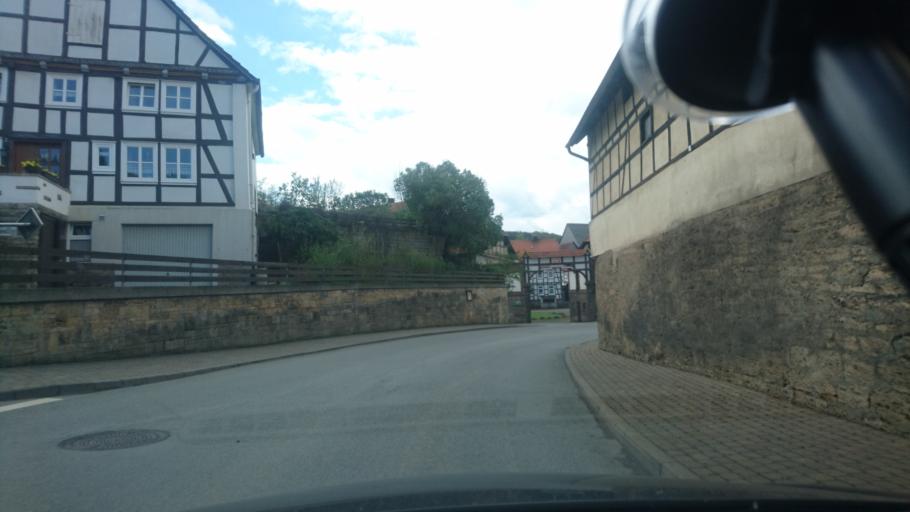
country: DE
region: Hesse
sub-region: Regierungsbezirk Kassel
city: Korbach
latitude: 51.3614
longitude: 8.8070
